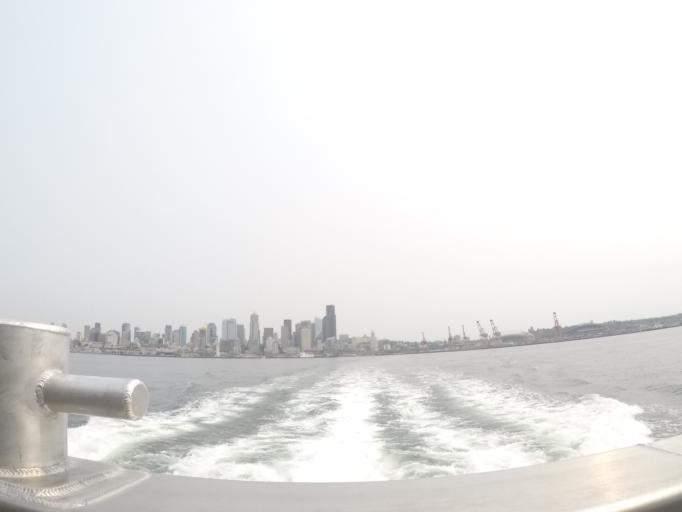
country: US
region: Washington
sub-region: King County
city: Seattle
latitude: 47.5963
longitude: -122.3614
